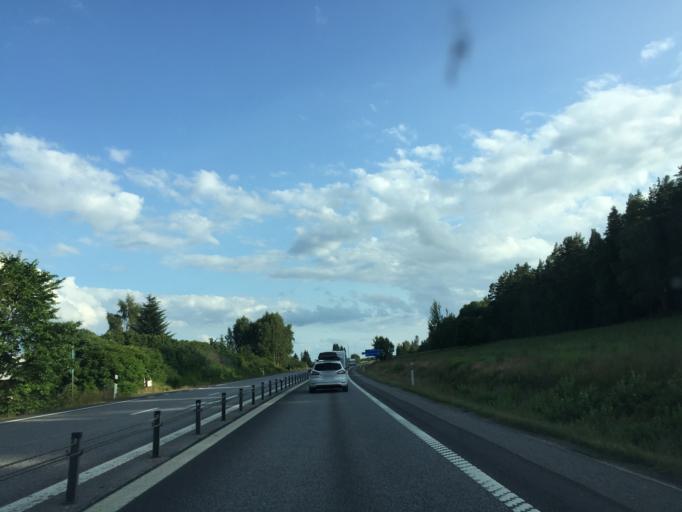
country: SE
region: OEstergoetland
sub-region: Motala Kommun
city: Motala
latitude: 58.5932
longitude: 14.9889
